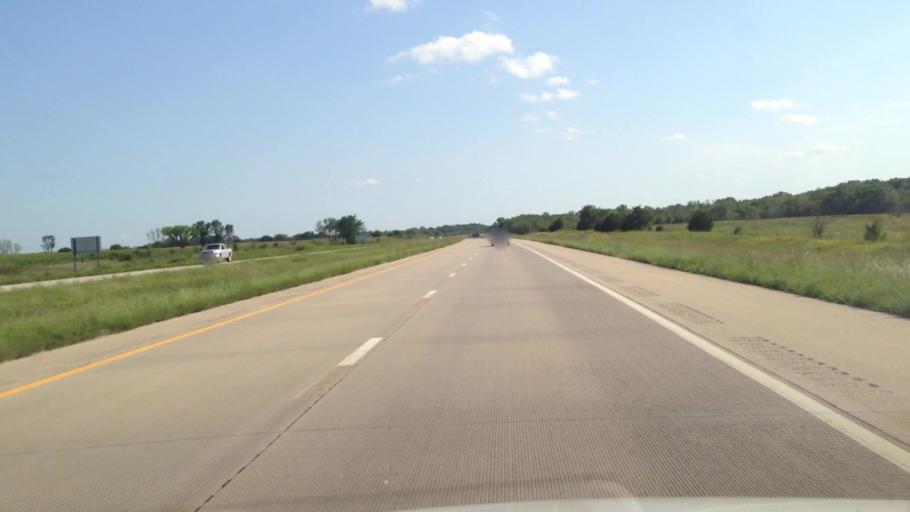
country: US
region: Kansas
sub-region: Bourbon County
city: Fort Scott
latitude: 37.9191
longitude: -94.7045
